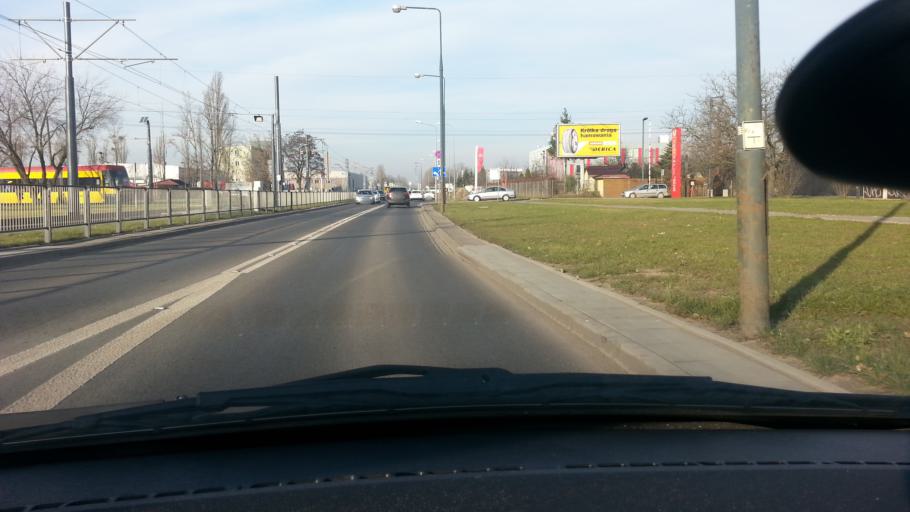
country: PL
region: Masovian Voivodeship
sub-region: Warszawa
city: Targowek
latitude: 52.2990
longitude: 21.0232
